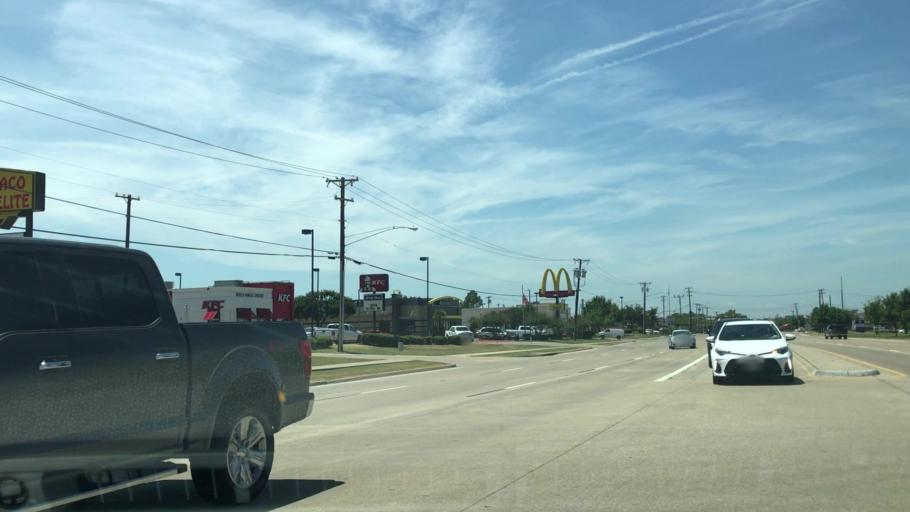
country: US
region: Texas
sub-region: Collin County
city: Wylie
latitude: 33.0093
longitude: -96.5439
